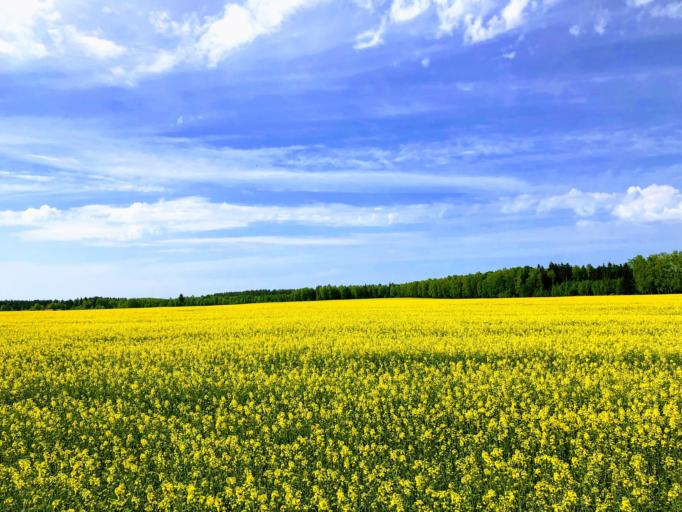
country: BY
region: Minsk
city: Kapyl'
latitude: 53.3070
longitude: 27.0792
